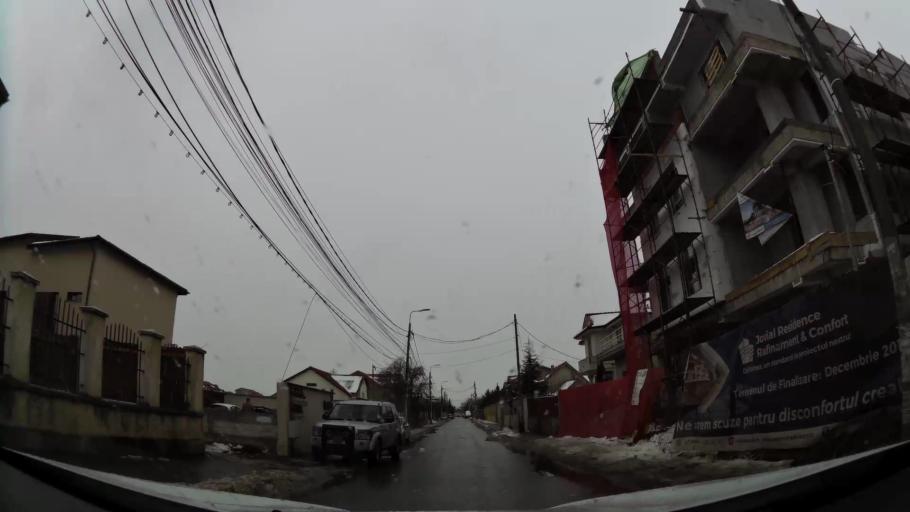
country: RO
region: Ilfov
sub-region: Comuna Chiajna
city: Rosu
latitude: 44.4099
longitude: 26.0106
